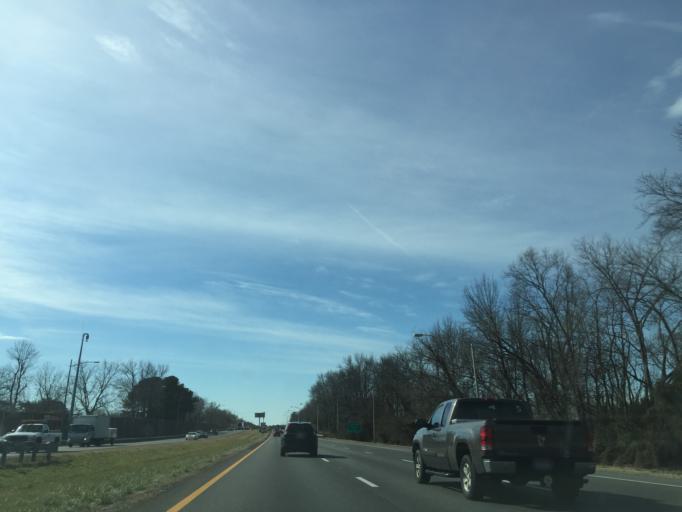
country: US
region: Virginia
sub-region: City of Hampton
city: East Hampton
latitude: 36.9538
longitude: -76.2647
